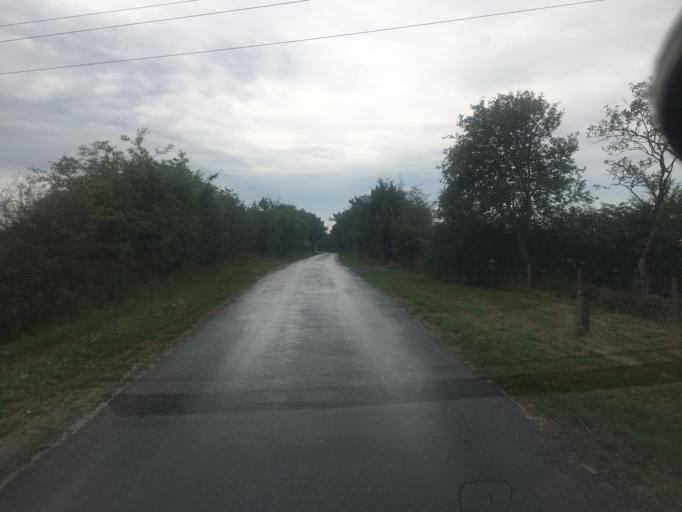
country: DK
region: South Denmark
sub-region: Tonder Kommune
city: Logumkloster
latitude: 55.0318
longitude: 8.9190
